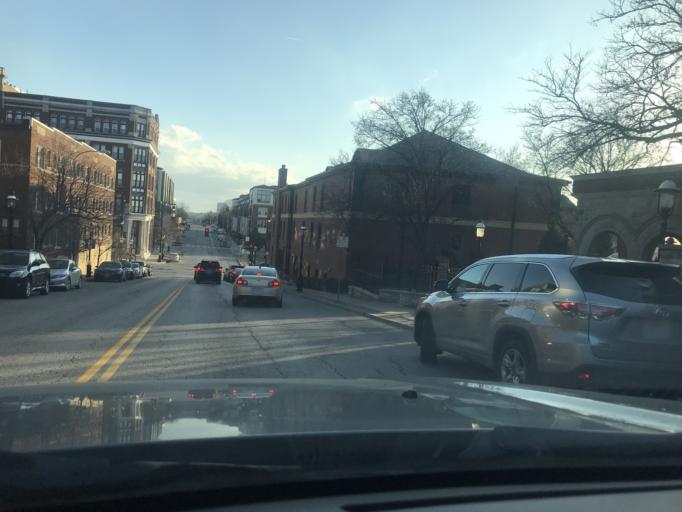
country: US
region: Missouri
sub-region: Jackson County
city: Kansas City
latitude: 39.1010
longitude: -94.5912
